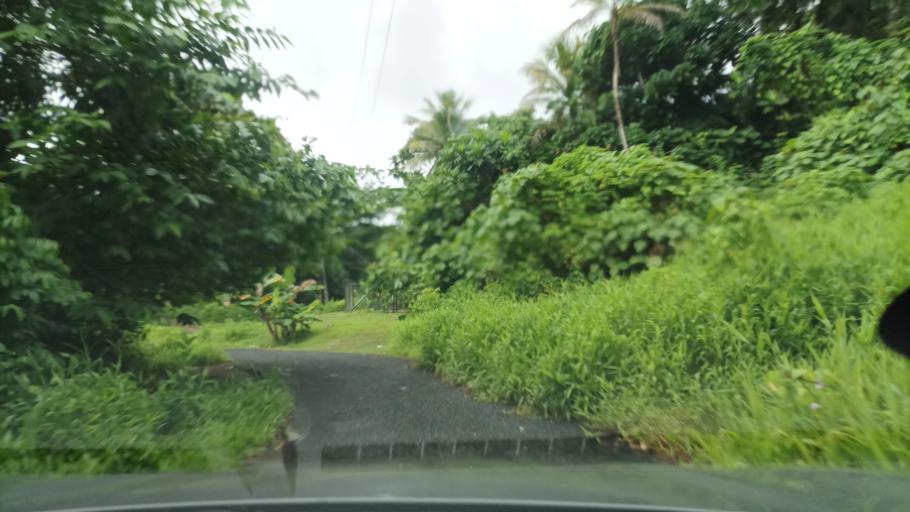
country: FM
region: Pohnpei
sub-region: Madolenihm Municipality
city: Madolenihm Municipality Government
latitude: 6.9146
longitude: 158.2909
